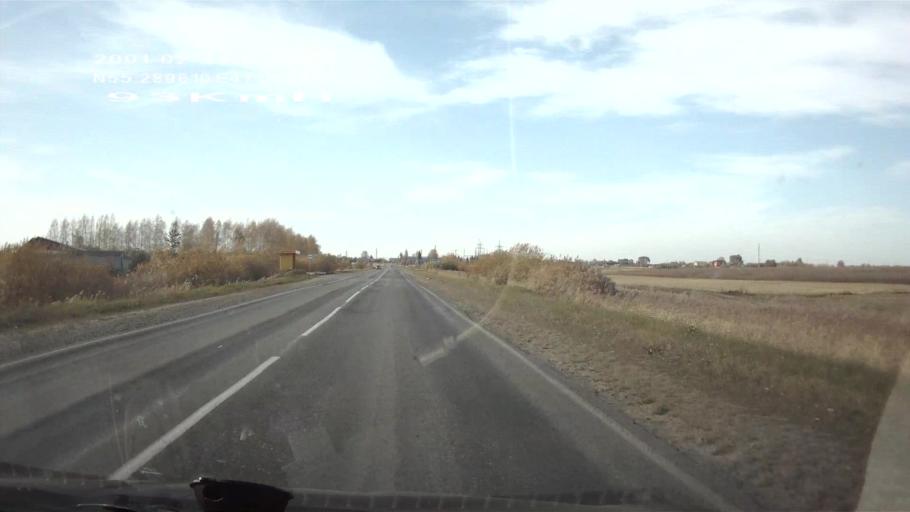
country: RU
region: Chuvashia
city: Ibresi
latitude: 55.2896
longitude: 47.0649
